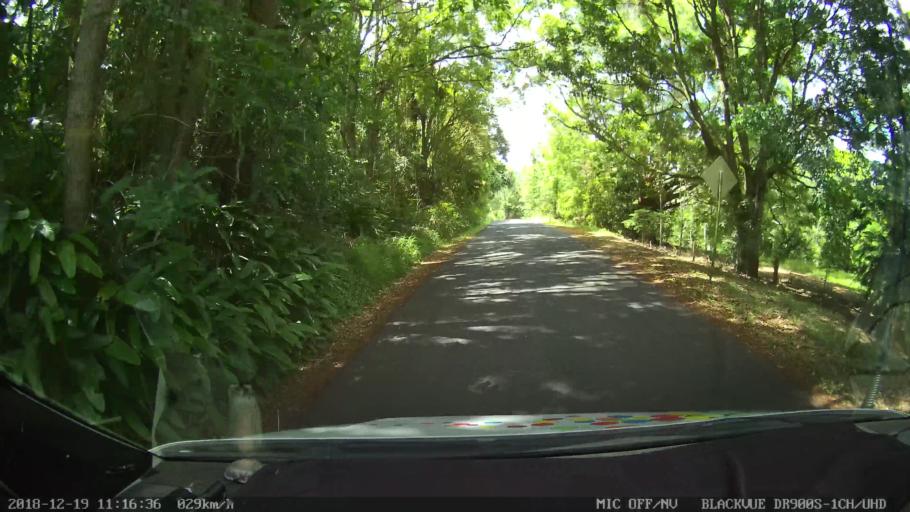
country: AU
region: New South Wales
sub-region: Lismore Municipality
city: Nimbin
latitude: -28.6746
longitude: 153.2784
